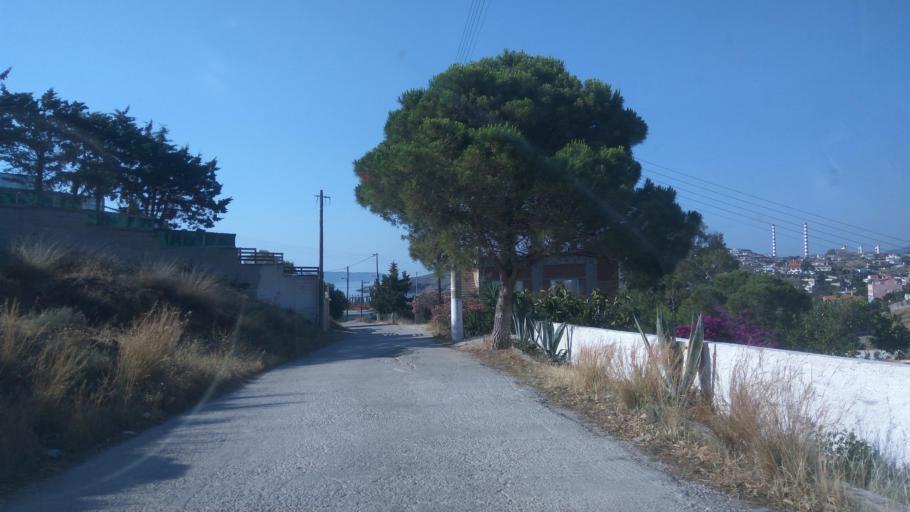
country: GR
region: Attica
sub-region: Nomarchia Anatolikis Attikis
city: Lavrio
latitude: 37.7654
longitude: 24.0744
